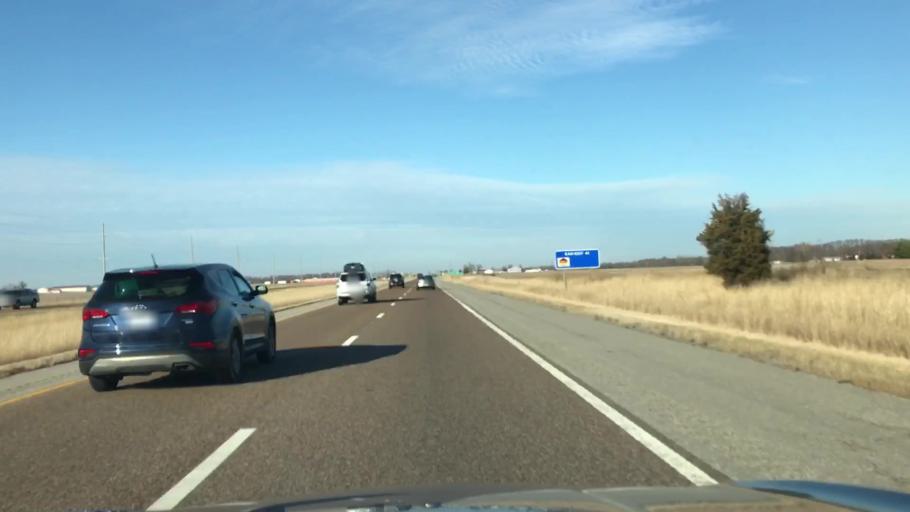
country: US
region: Illinois
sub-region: Macoupin County
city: Staunton
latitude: 38.9943
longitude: -89.7493
